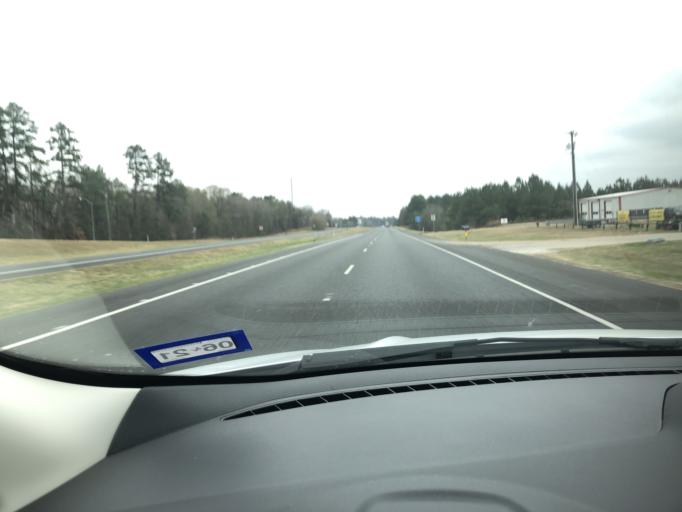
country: US
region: Texas
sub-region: Nacogdoches County
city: Nacogdoches
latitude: 31.5335
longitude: -94.6941
